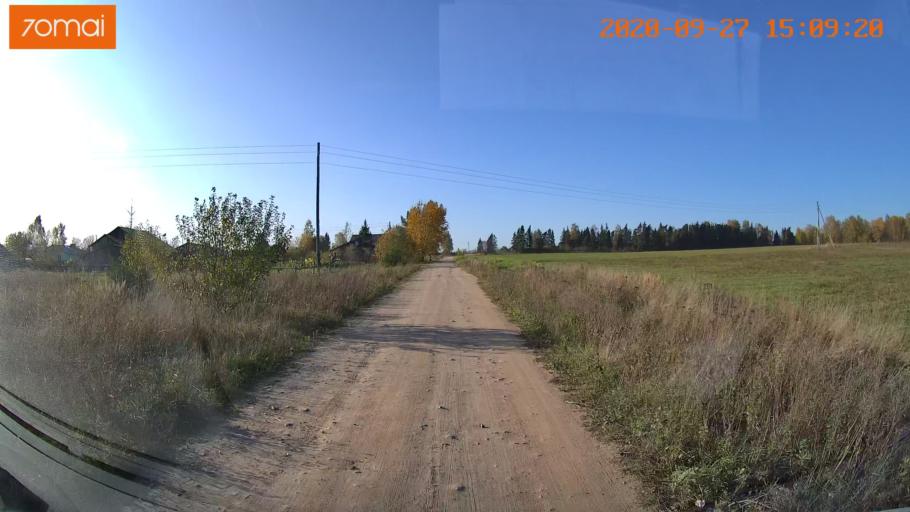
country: RU
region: Ivanovo
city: Furmanov
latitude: 57.1640
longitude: 41.0748
